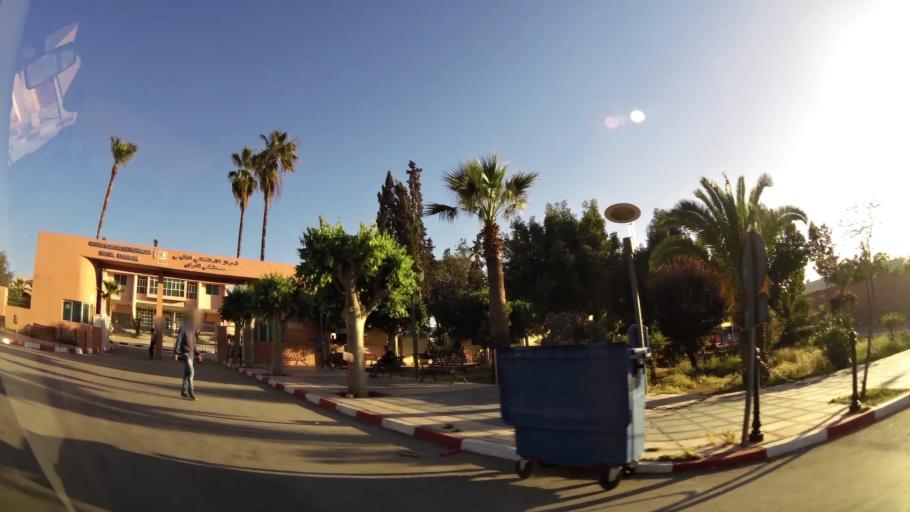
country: MA
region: Oriental
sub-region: Berkane-Taourirt
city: Berkane
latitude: 34.9259
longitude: -2.3253
